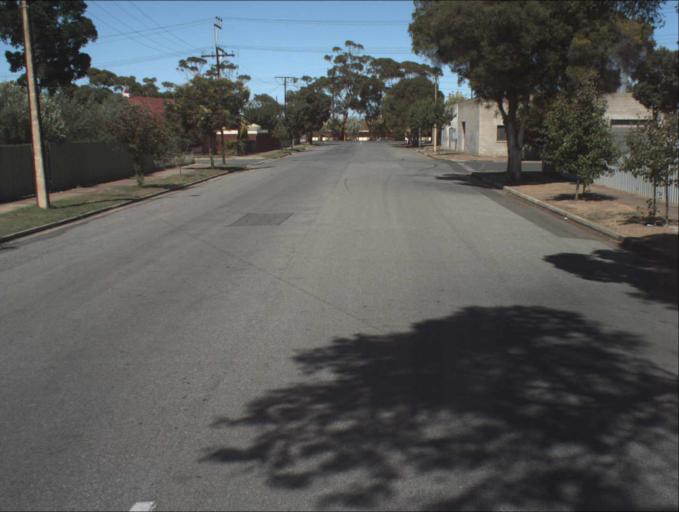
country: AU
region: South Australia
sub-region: Port Adelaide Enfield
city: Cheltenham
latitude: -34.8653
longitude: 138.5181
